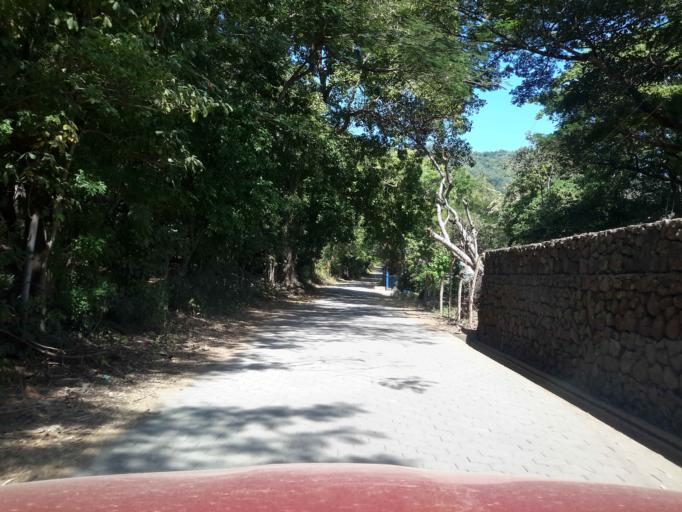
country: NI
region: Masaya
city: Catarina
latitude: 11.9353
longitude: -86.0540
